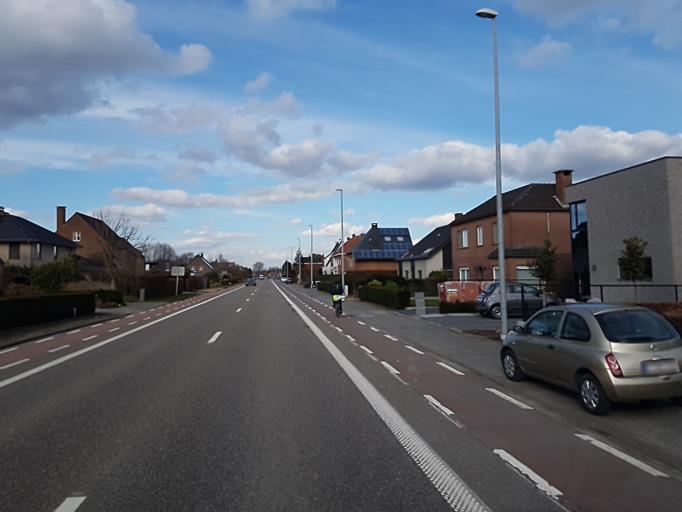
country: BE
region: Flanders
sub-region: Provincie Oost-Vlaanderen
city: Sint-Niklaas
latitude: 51.1838
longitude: 4.1606
